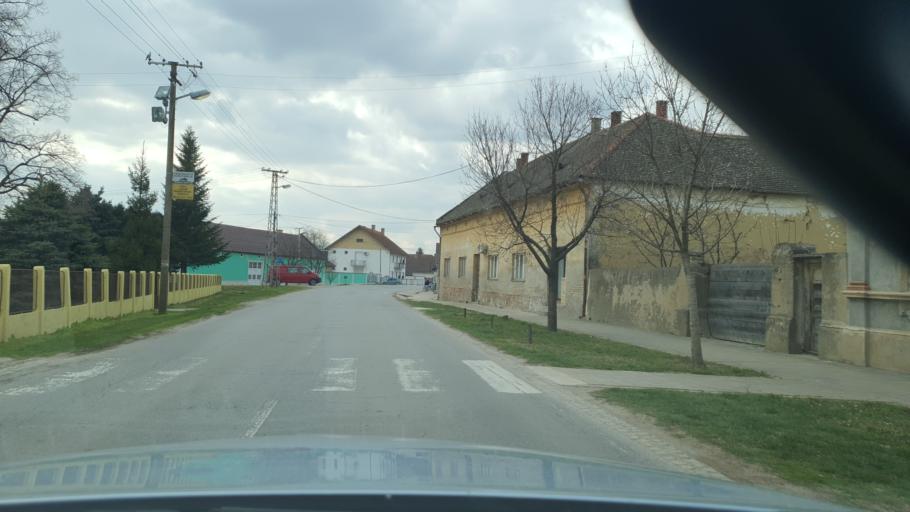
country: RS
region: Autonomna Pokrajina Vojvodina
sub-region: Juznobacki Okrug
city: Bac
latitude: 45.4078
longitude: 19.2947
